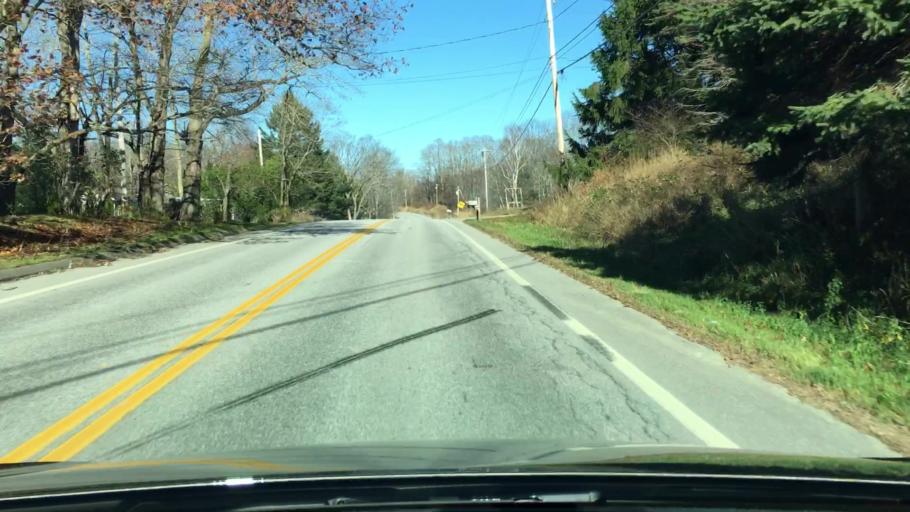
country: US
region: Maine
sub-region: Waldo County
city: Winterport
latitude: 44.6382
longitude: -68.8286
